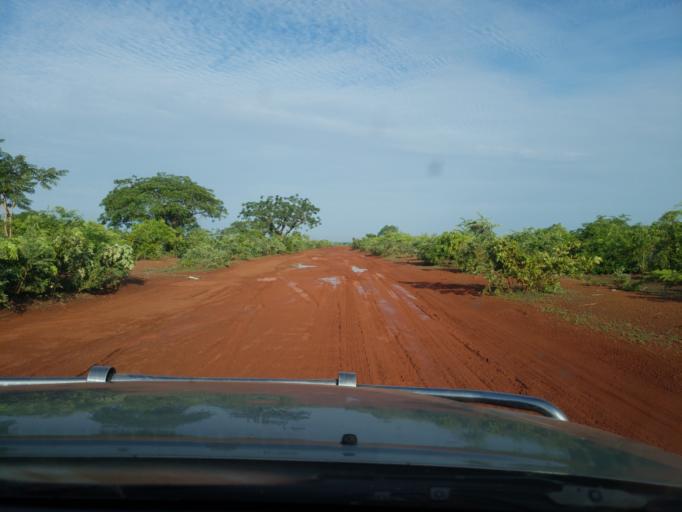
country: ML
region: Sikasso
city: Koutiala
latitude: 12.4266
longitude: -5.6405
